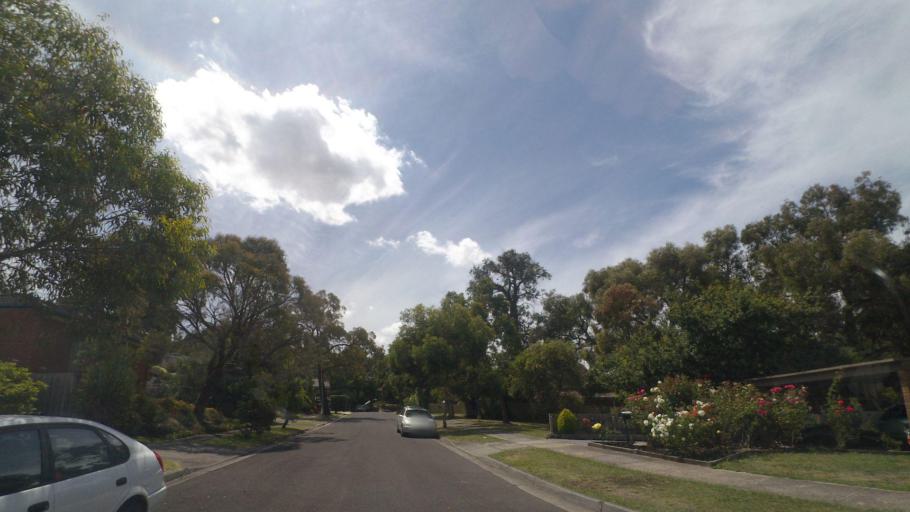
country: AU
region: Victoria
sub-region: Maroondah
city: Bayswater North
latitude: -37.8404
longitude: 145.2945
